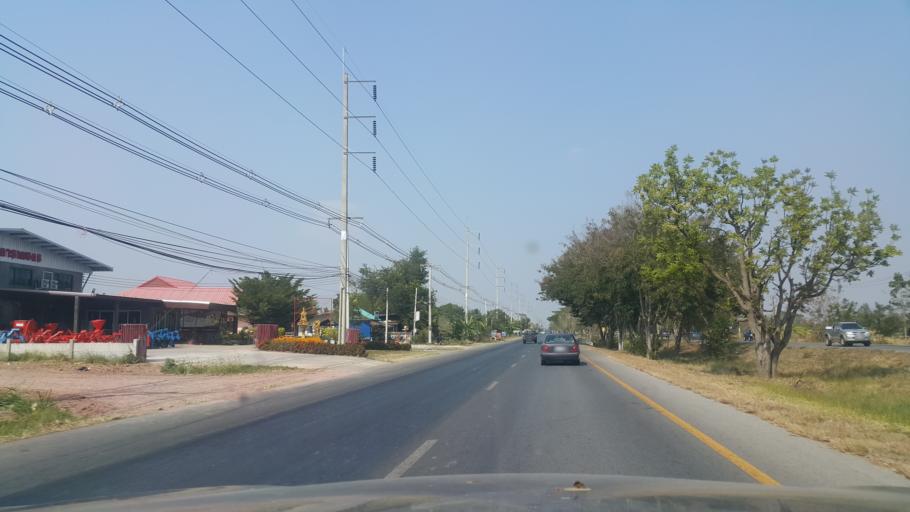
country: TH
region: Nakhon Ratchasima
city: Pak Thong Chai
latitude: 14.6553
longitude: 102.0123
